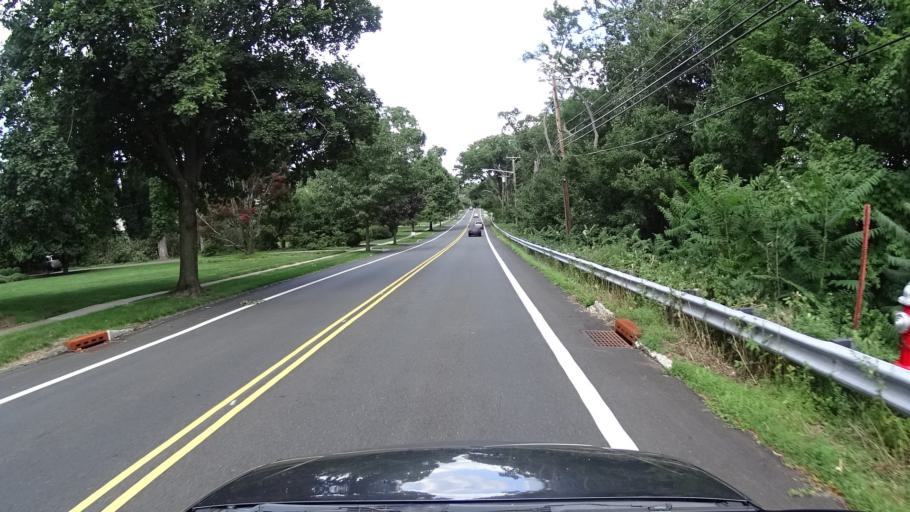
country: US
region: New Jersey
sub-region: Morris County
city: Chatham
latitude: 40.7287
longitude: -74.3926
